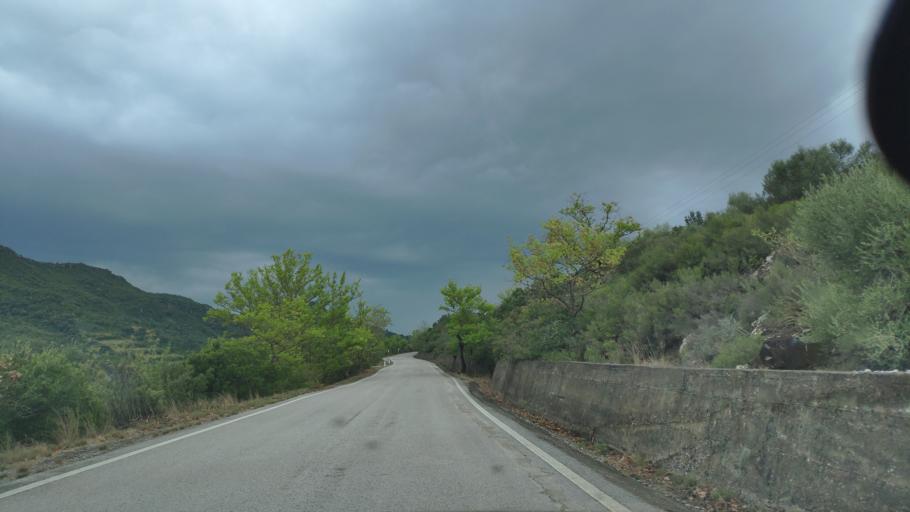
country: GR
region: West Greece
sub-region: Nomos Aitolias kai Akarnanias
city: Lepenou
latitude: 38.8152
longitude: 21.3346
